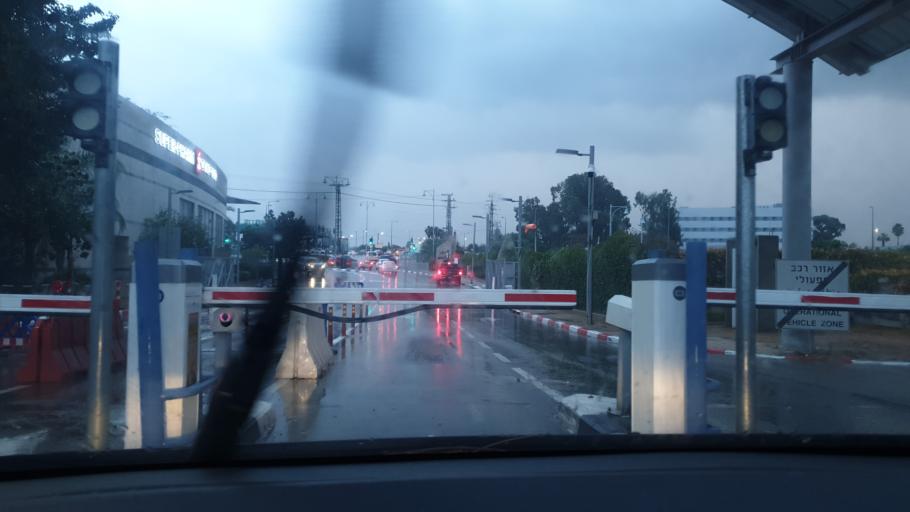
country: IL
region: Central District
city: Kefar Habad
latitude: 31.9679
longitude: 34.8428
